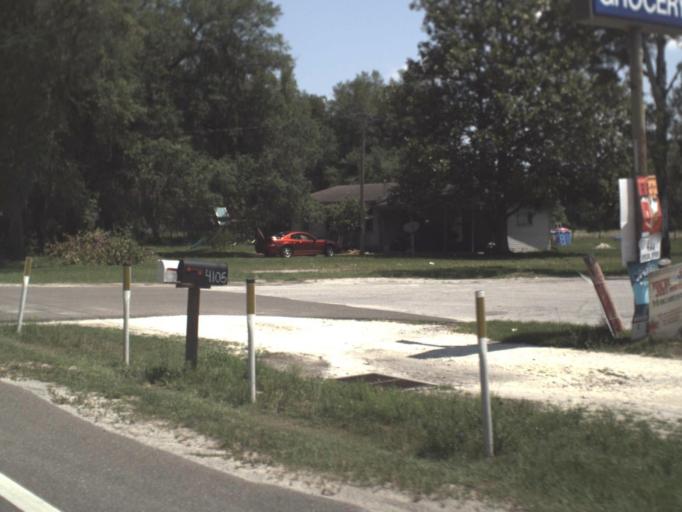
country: US
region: Florida
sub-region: Clay County
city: Keystone Heights
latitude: 29.8420
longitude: -82.0661
